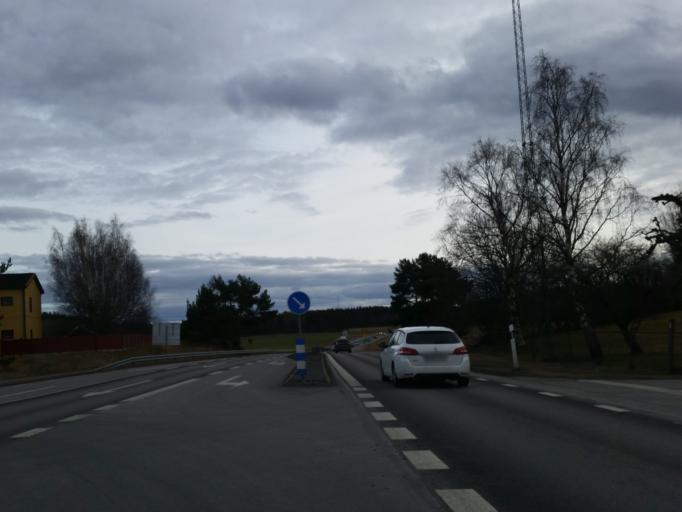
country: SE
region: OEstergoetland
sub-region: Soderkopings Kommun
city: Soederkoeping
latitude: 58.5302
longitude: 16.2864
